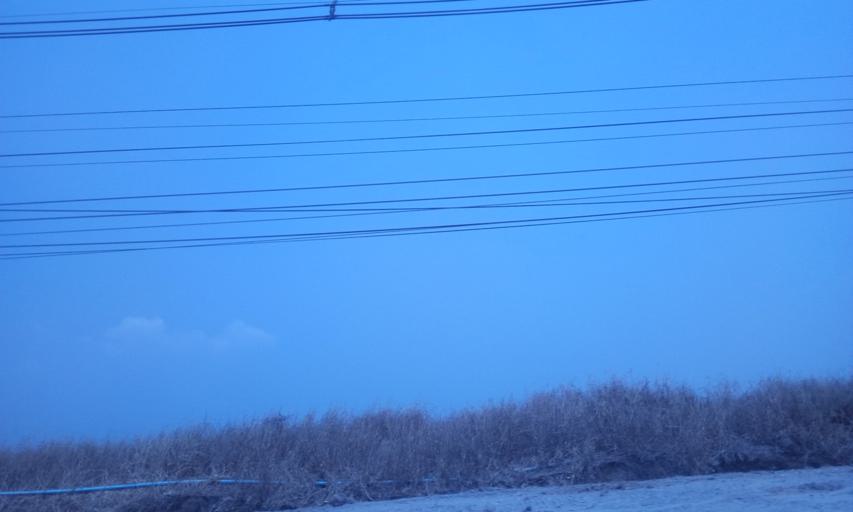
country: TH
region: Chachoengsao
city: Ban Pho
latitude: 13.5431
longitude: 101.1454
